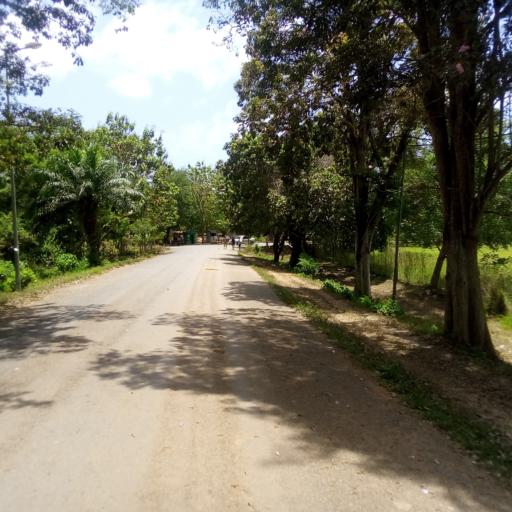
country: GH
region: Central
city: Cape Coast
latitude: 5.1310
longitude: -1.2907
